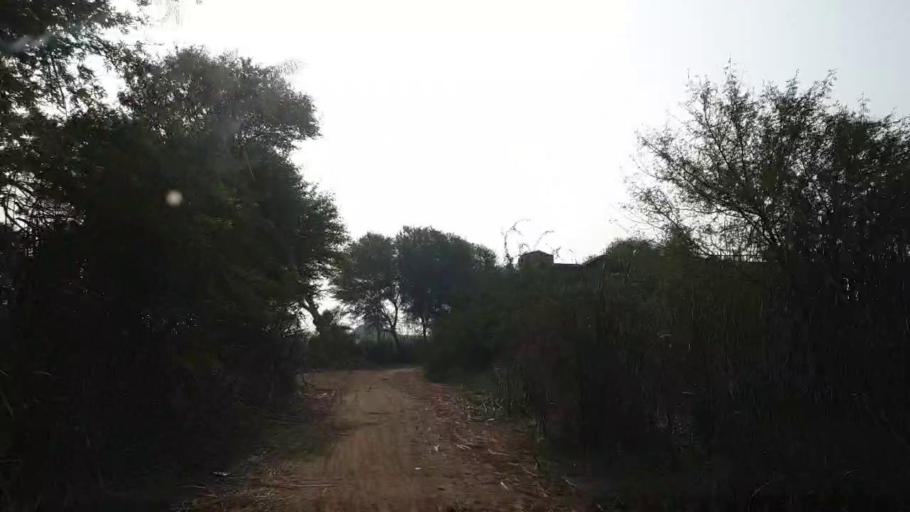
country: PK
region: Sindh
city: Matli
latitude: 25.0672
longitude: 68.6090
